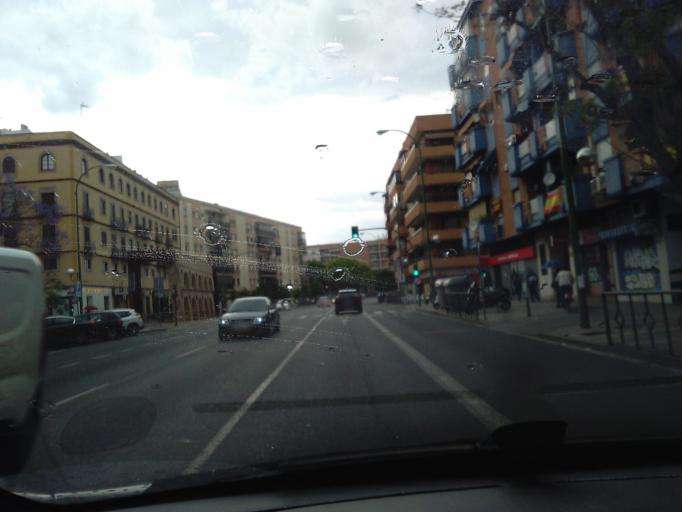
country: ES
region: Andalusia
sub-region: Provincia de Sevilla
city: Sevilla
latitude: 37.3878
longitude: -5.9805
